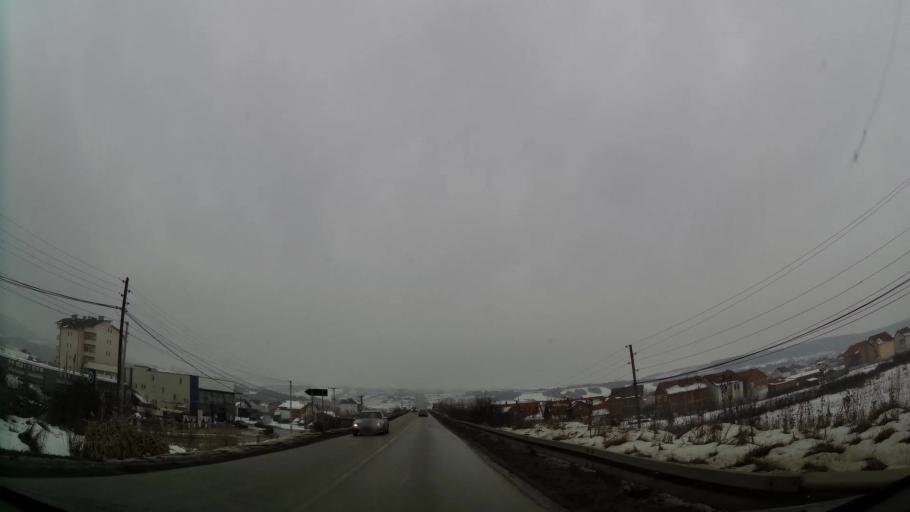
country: XK
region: Pristina
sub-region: Komuna e Prishtines
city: Pristina
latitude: 42.7123
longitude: 21.1515
